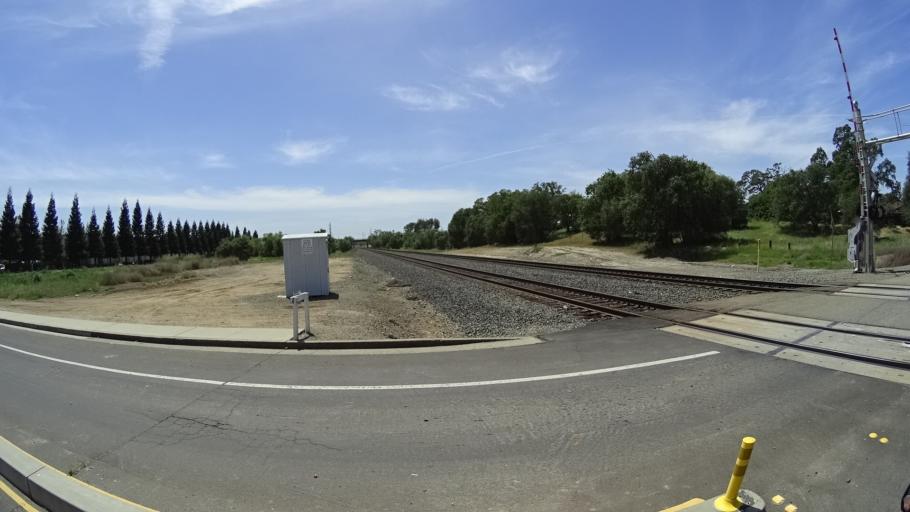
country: US
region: California
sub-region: Placer County
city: Rocklin
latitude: 38.7865
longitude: -121.2408
